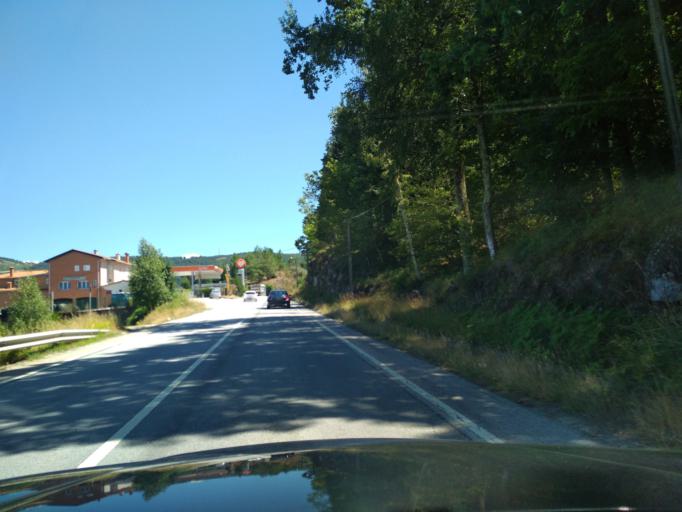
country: PT
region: Vila Real
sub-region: Ribeira de Pena
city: Ribeira de Pena
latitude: 41.5168
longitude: -7.8042
